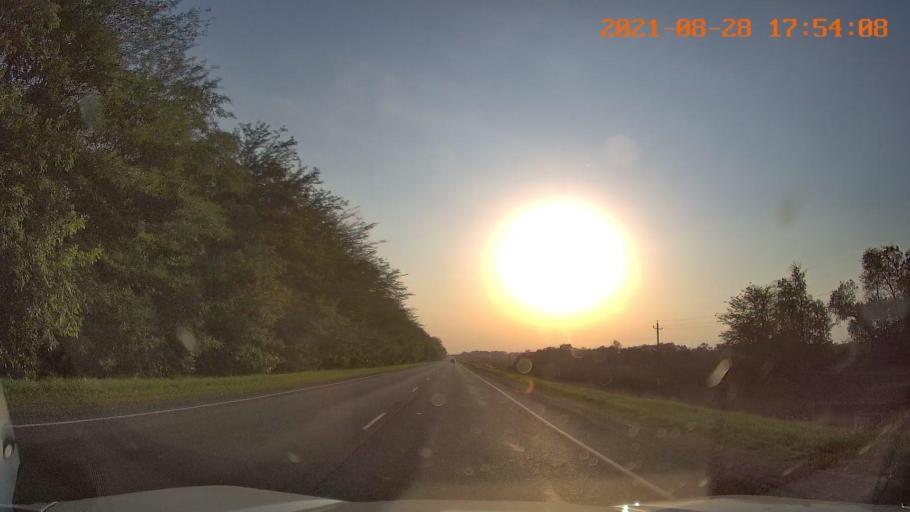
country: RU
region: Krasnodarskiy
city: Konstantinovskaya
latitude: 44.9364
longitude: 40.7432
